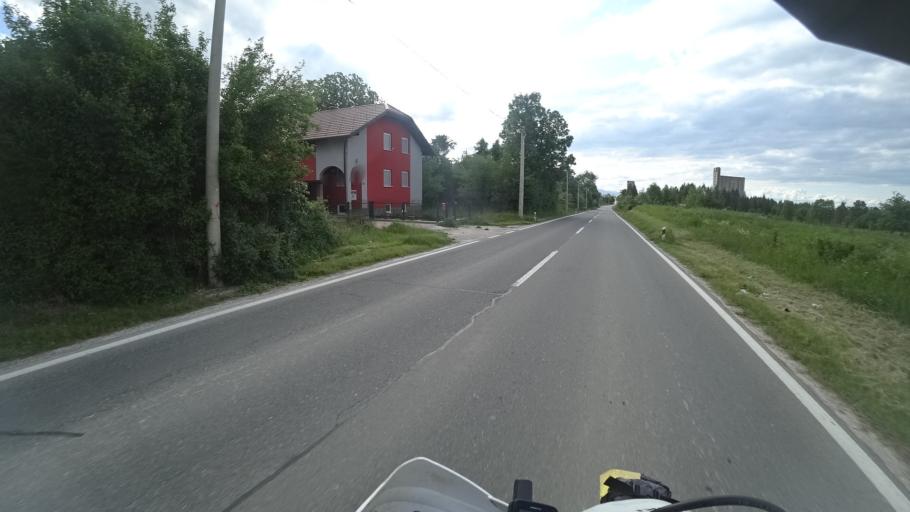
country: HR
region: Licko-Senjska
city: Gospic
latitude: 44.5306
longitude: 15.4024
